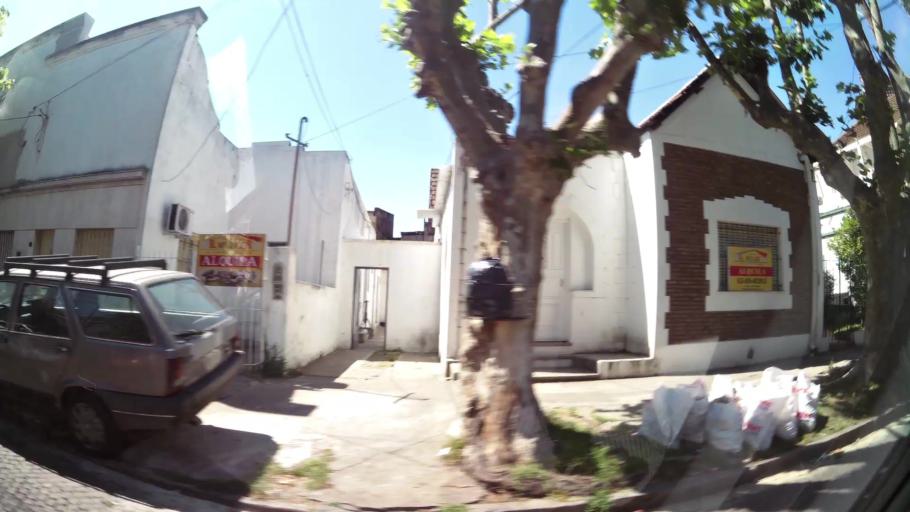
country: AR
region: Buenos Aires
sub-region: Partido de Tigre
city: Tigre
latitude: -34.4323
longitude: -58.5672
